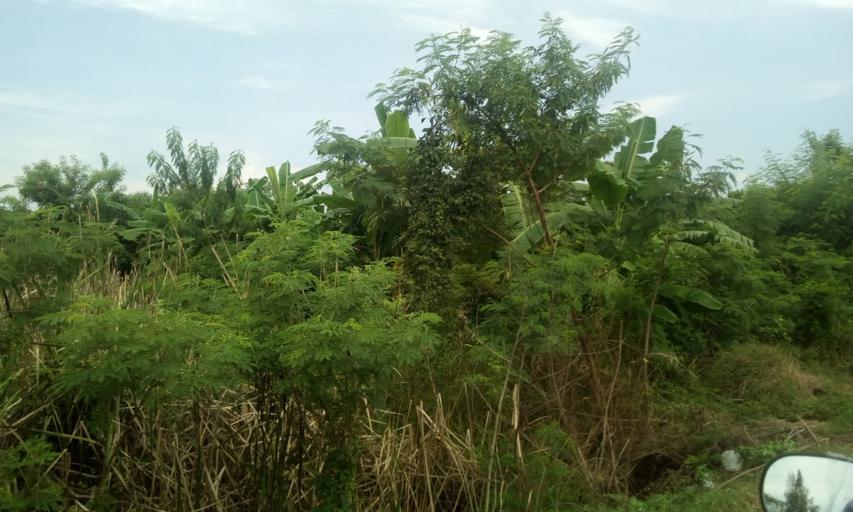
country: TH
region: Pathum Thani
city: Ban Lam Luk Ka
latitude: 14.0040
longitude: 100.8422
